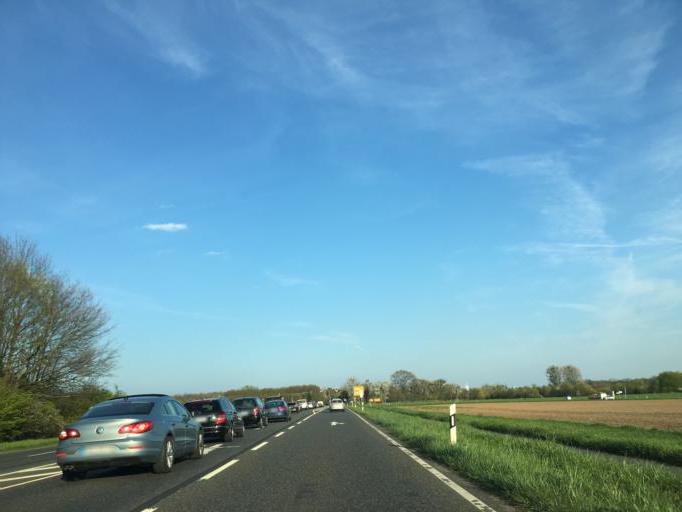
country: DE
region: Hesse
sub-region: Regierungsbezirk Darmstadt
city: Maintal
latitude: 50.1377
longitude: 8.7994
